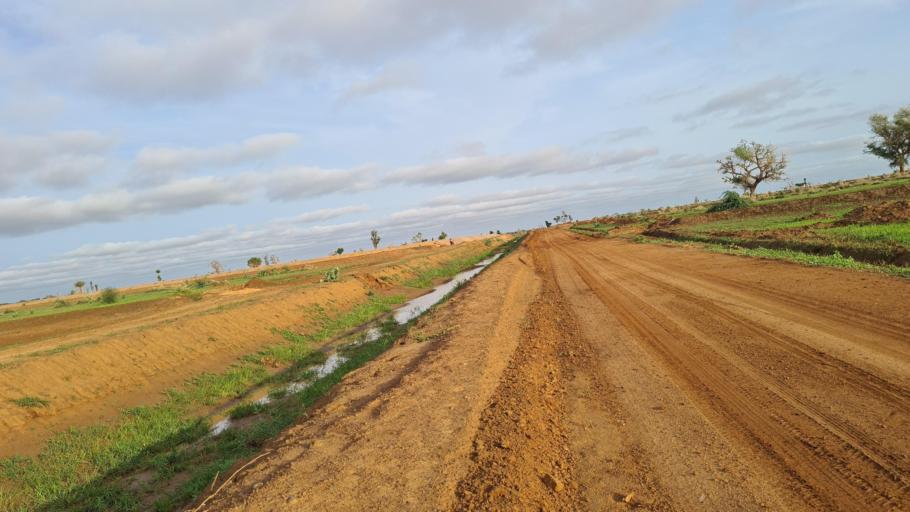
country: NE
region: Tahoua
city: Birni N Konni
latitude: 13.7870
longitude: 5.2311
